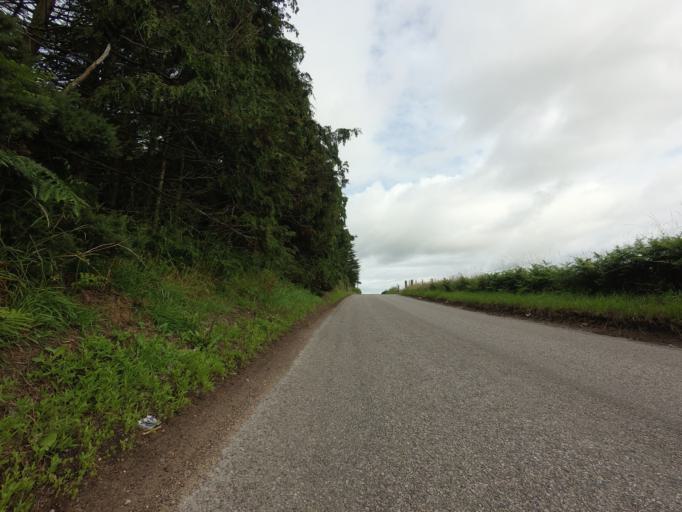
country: GB
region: Scotland
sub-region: Moray
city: Elgin
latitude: 57.6592
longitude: -3.3543
